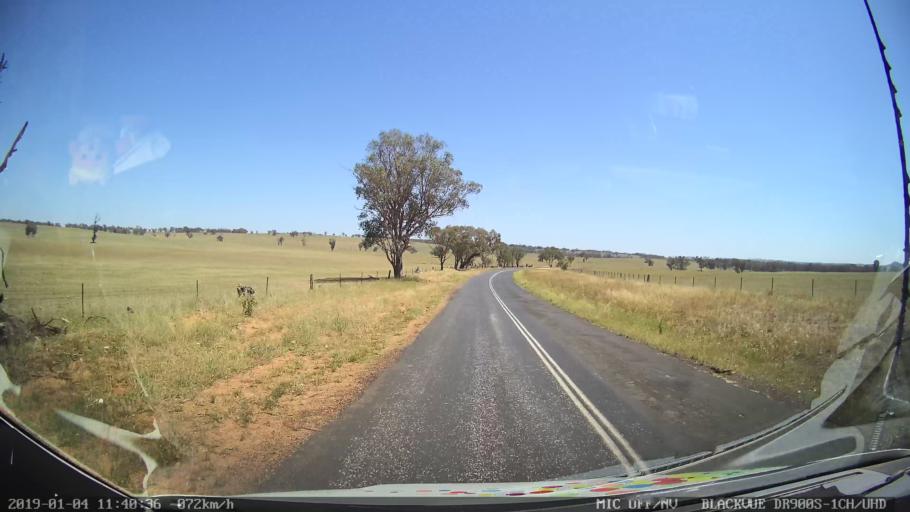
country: AU
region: New South Wales
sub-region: Cabonne
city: Molong
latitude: -33.0035
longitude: 148.7864
